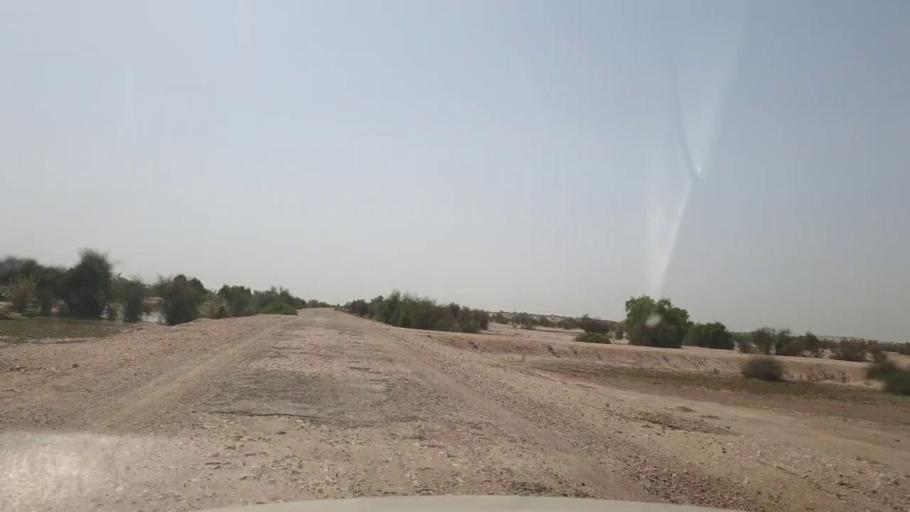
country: PK
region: Sindh
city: Rohri
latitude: 27.4437
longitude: 69.2382
